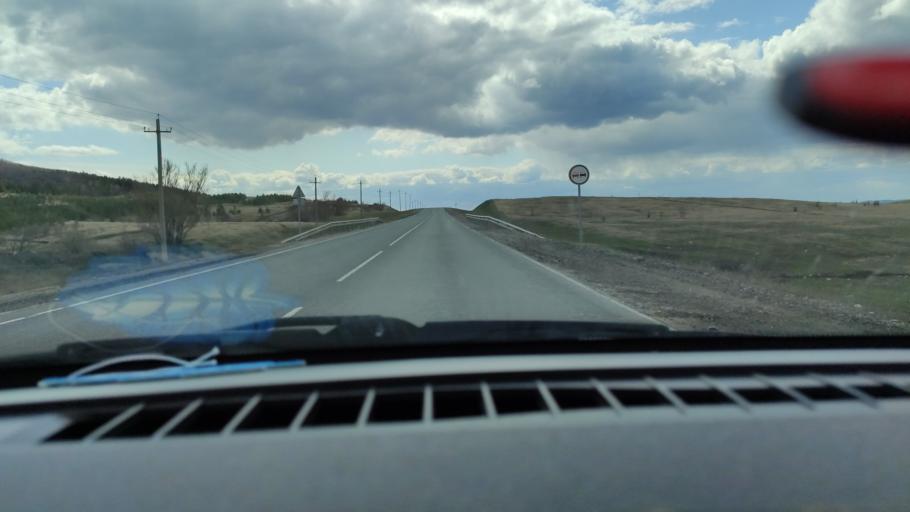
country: RU
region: Saratov
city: Alekseyevka
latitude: 52.3002
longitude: 47.9273
